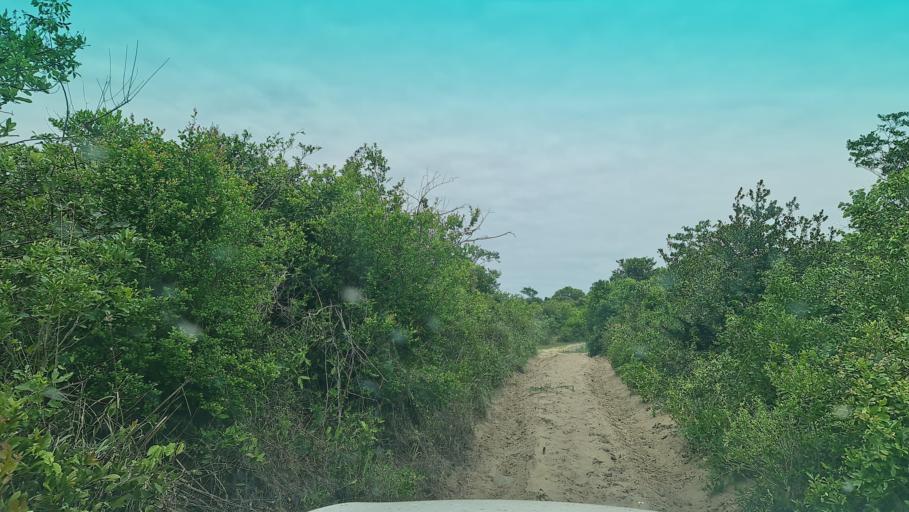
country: MZ
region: Maputo
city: Manhica
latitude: -25.6372
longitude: 32.7746
